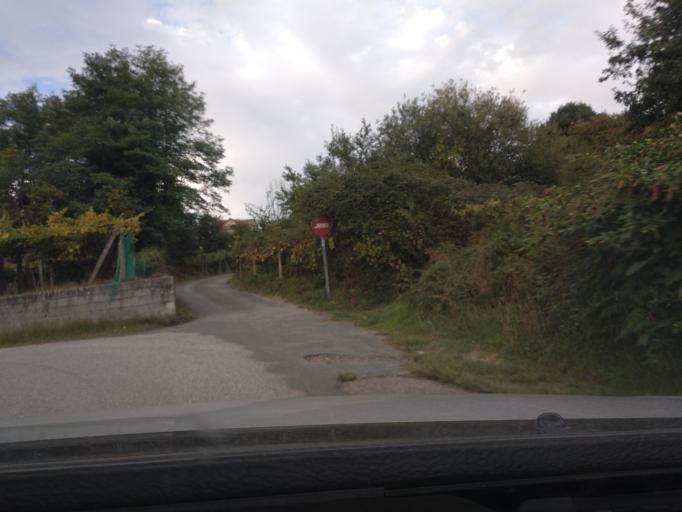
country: ES
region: Galicia
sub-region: Provincia de Pontevedra
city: Moana
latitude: 42.2970
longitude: -8.7344
